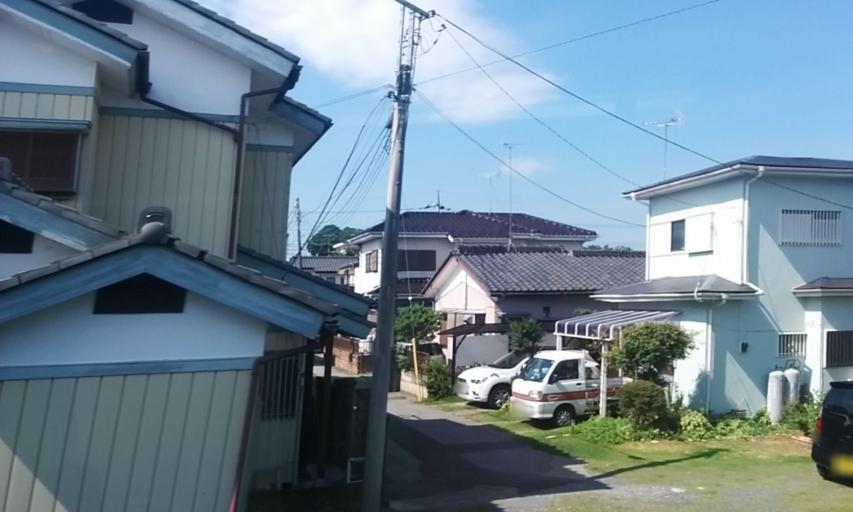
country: JP
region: Saitama
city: Kazo
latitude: 36.1361
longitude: 139.5763
